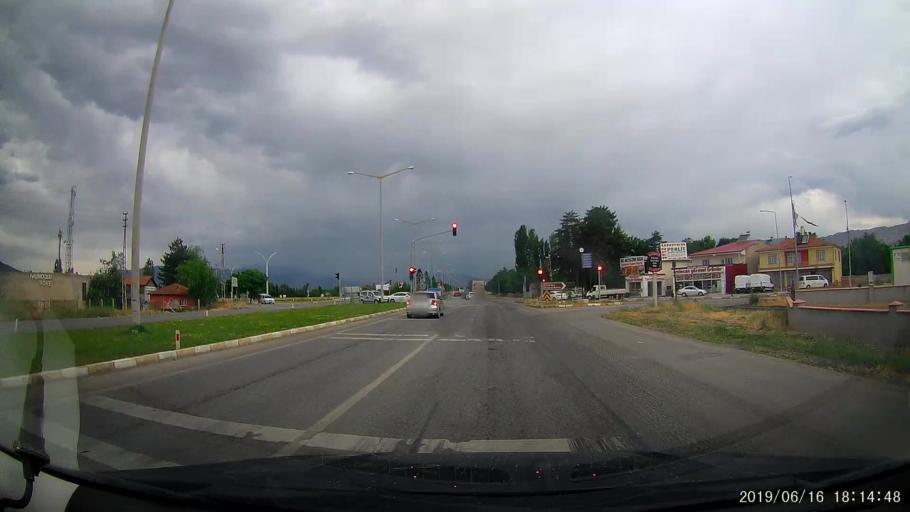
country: TR
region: Erzincan
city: Erzincan
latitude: 39.7263
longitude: 39.5533
